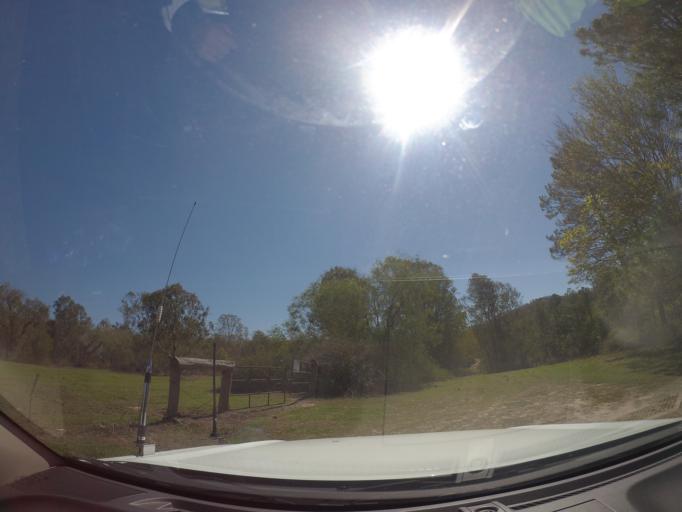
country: AU
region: Queensland
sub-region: Ipswich
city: Springfield Lakes
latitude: -27.7542
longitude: 152.8791
